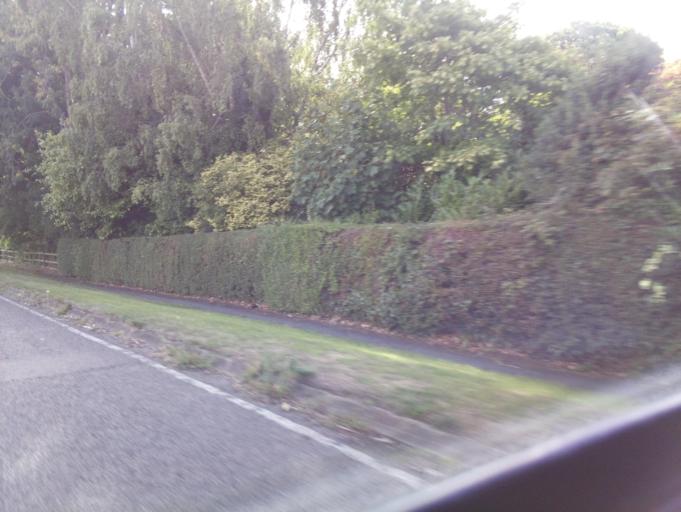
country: GB
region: England
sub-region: Leicestershire
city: Ashby de la Zouch
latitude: 52.7326
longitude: -1.4854
